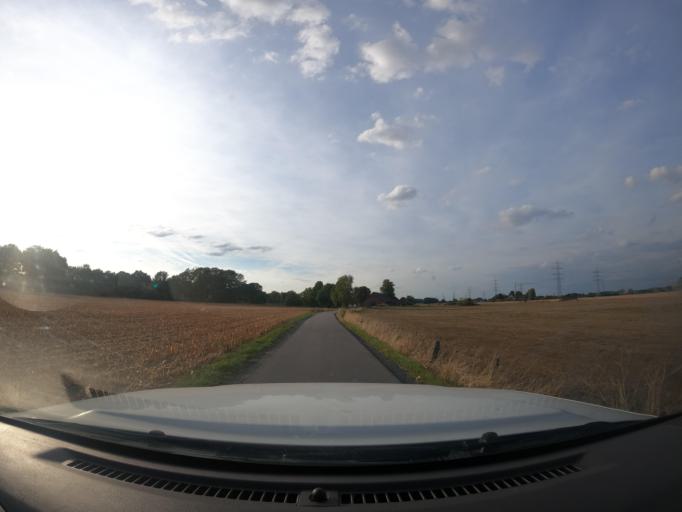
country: DE
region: North Rhine-Westphalia
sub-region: Regierungsbezirk Dusseldorf
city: Hamminkeln
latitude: 51.7053
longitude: 6.5836
